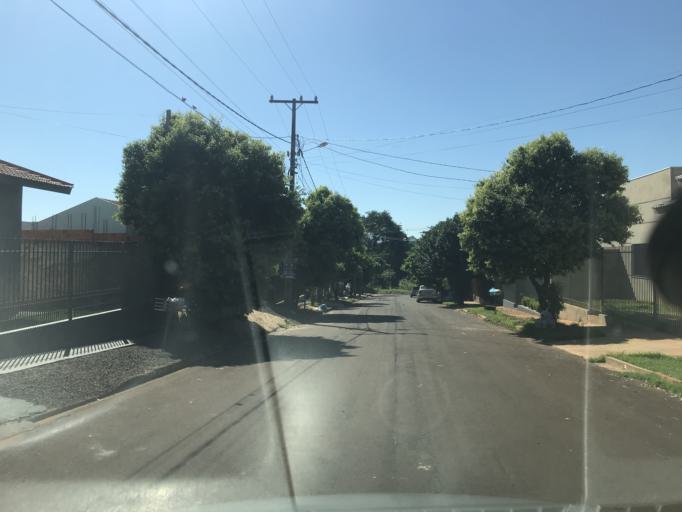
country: BR
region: Parana
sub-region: Palotina
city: Palotina
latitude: -24.2772
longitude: -53.8255
